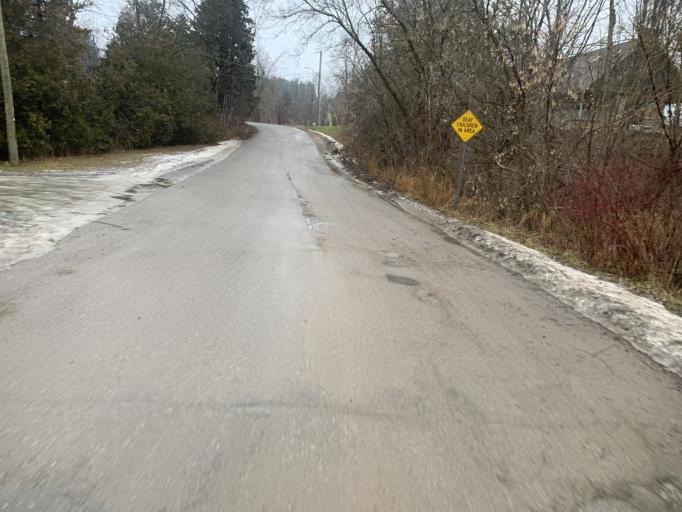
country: CA
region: Ontario
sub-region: Halton
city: Milton
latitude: 43.6582
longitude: -79.9338
